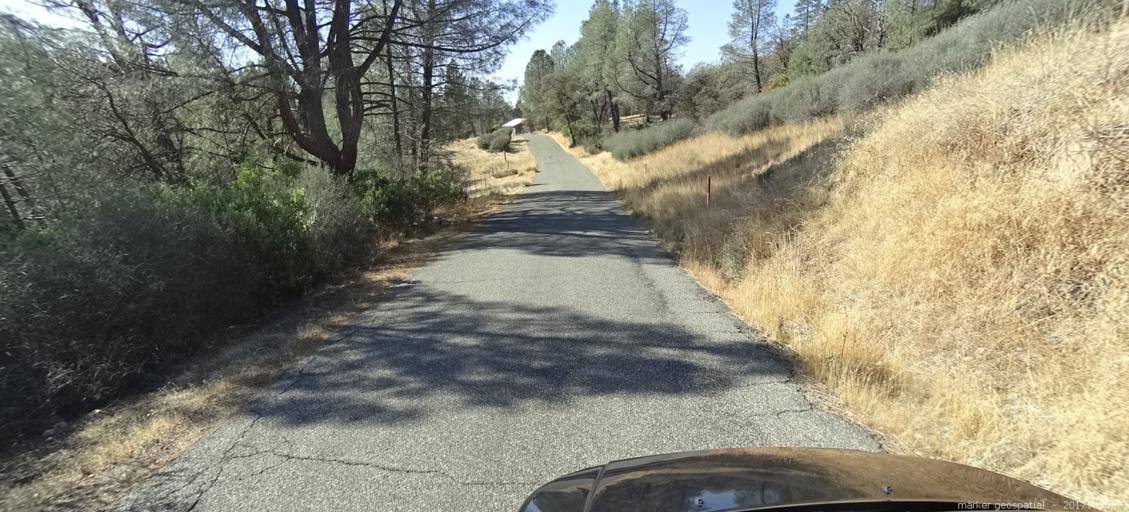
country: US
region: California
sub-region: Shasta County
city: Shingletown
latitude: 40.5826
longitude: -121.8711
